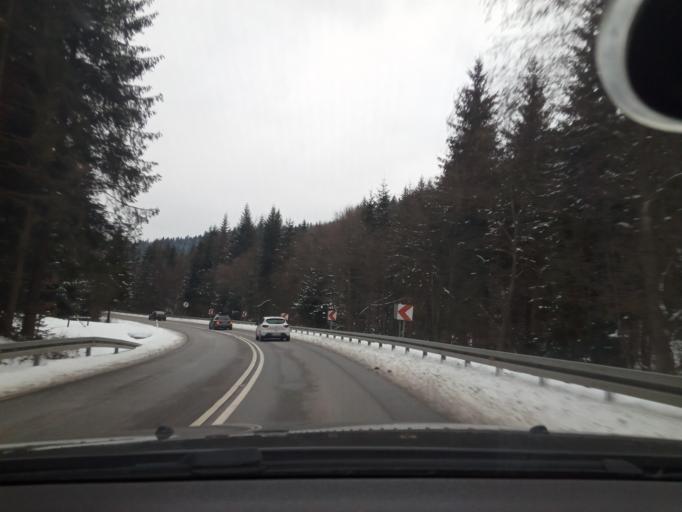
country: PL
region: Lesser Poland Voivodeship
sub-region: Powiat limanowski
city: Lubomierz
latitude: 49.6140
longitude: 20.2376
